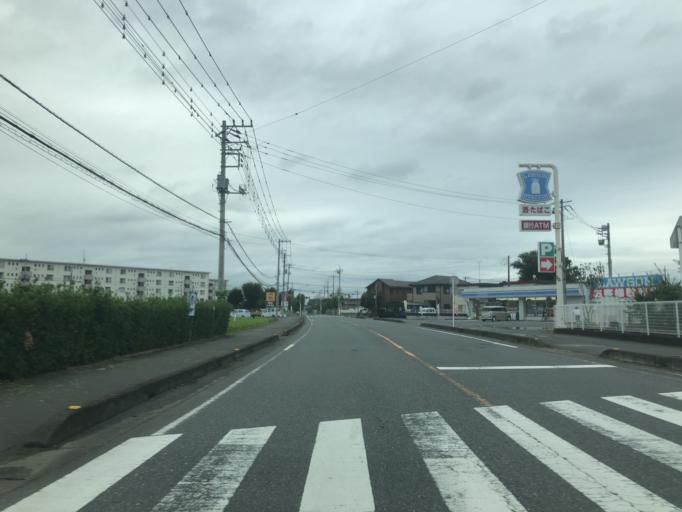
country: JP
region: Saitama
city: Sakado
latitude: 35.9796
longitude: 139.3957
